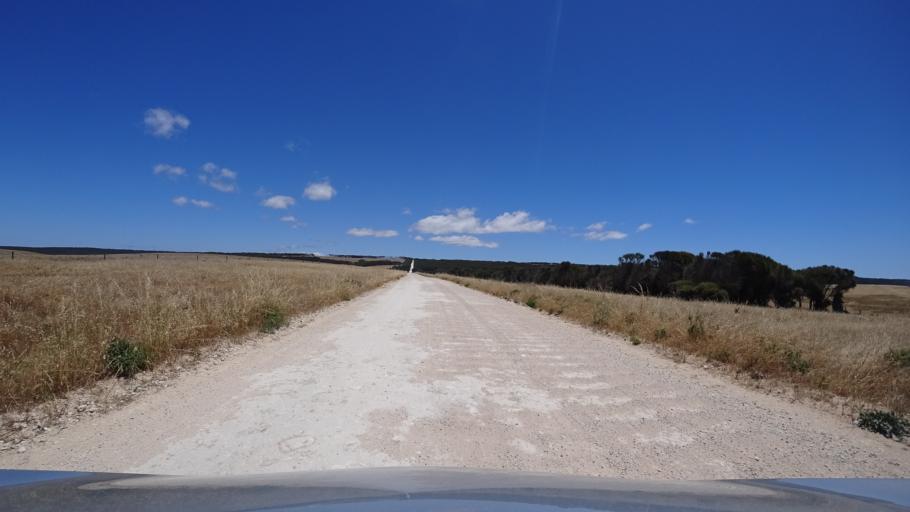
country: AU
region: South Australia
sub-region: Yankalilla
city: Normanville
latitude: -35.8410
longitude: 138.1260
